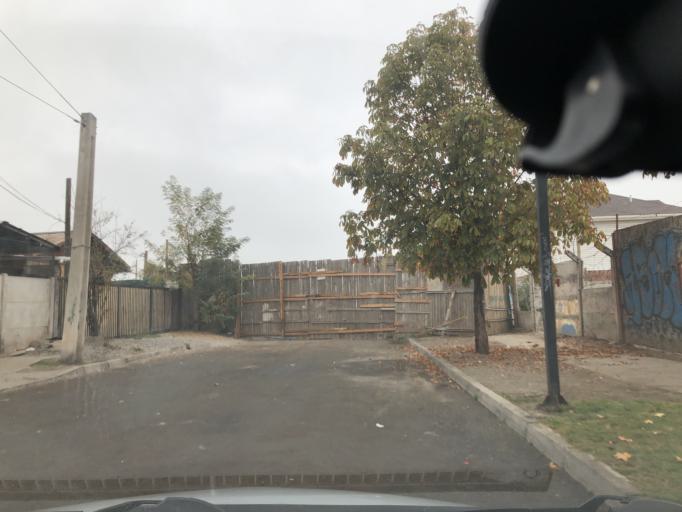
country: CL
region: Santiago Metropolitan
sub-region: Provincia de Cordillera
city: Puente Alto
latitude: -33.6022
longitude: -70.5915
